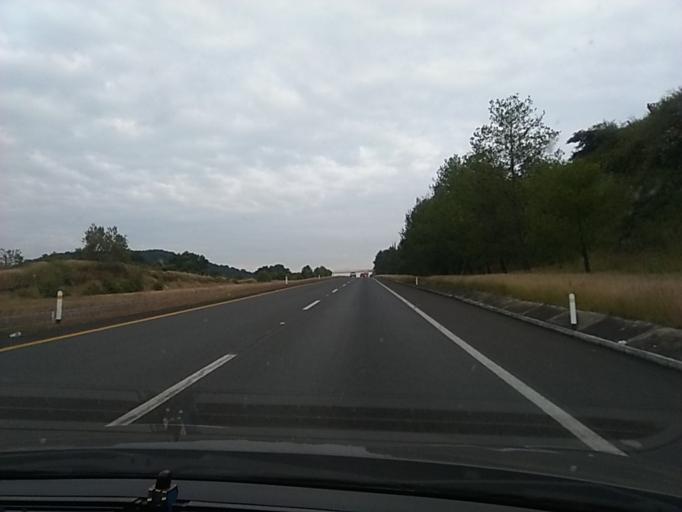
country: MX
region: Michoacan
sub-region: Puruandiro
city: San Lorenzo
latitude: 19.9604
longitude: -101.6800
